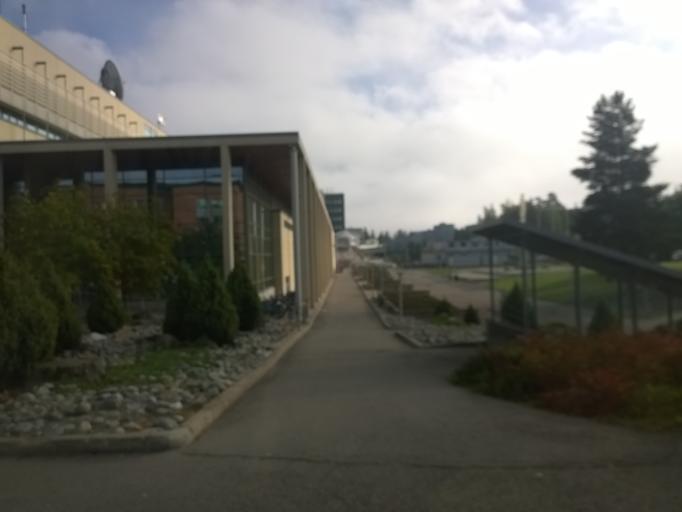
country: FI
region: Pirkanmaa
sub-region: Tampere
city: Tampere
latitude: 61.4494
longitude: 23.8544
